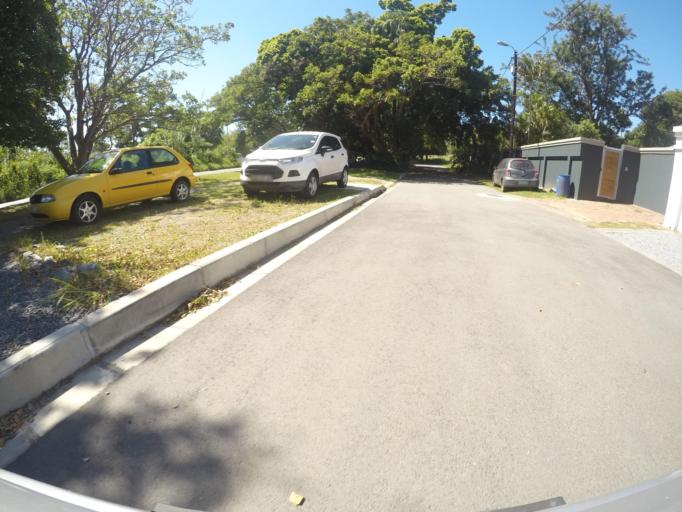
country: ZA
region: Eastern Cape
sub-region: Buffalo City Metropolitan Municipality
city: East London
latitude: -32.9725
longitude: 27.9235
